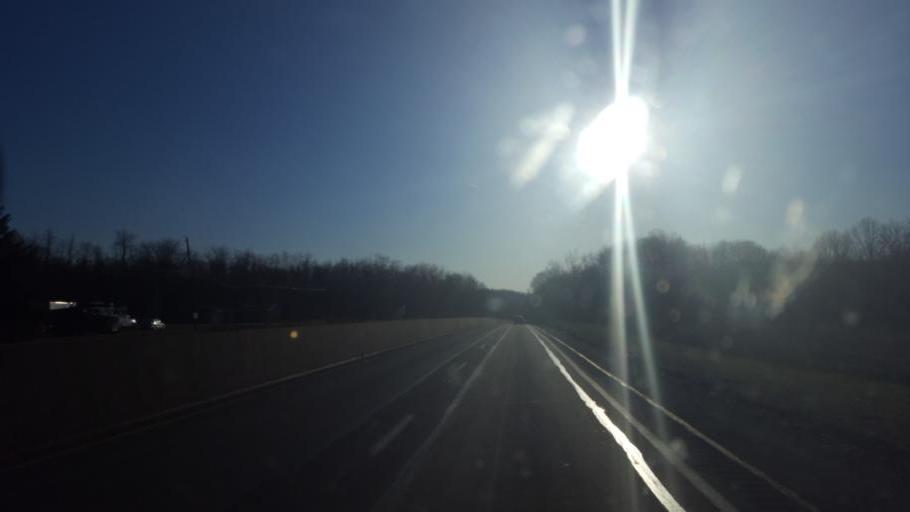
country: US
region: Pennsylvania
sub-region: Westmoreland County
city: New Stanton
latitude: 40.2142
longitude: -79.6419
